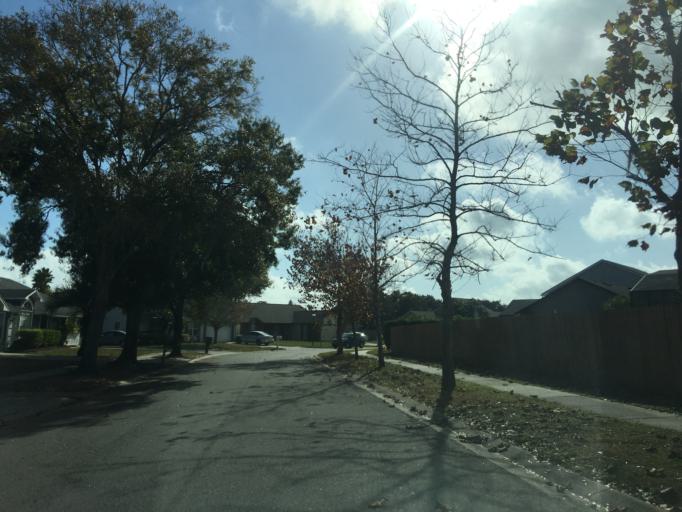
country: US
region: Florida
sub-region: Orange County
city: Azalea Park
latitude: 28.5176
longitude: -81.2765
